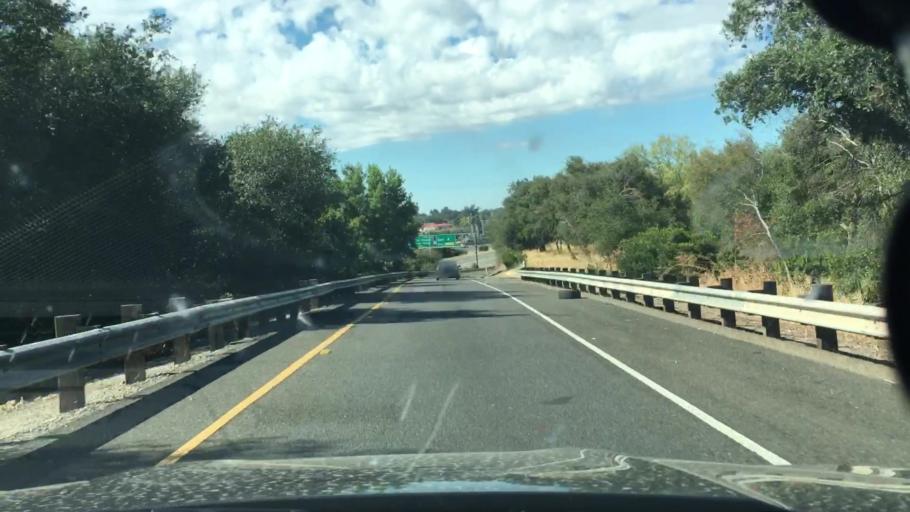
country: US
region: California
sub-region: Sacramento County
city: North Highlands
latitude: 38.6477
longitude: -121.3765
